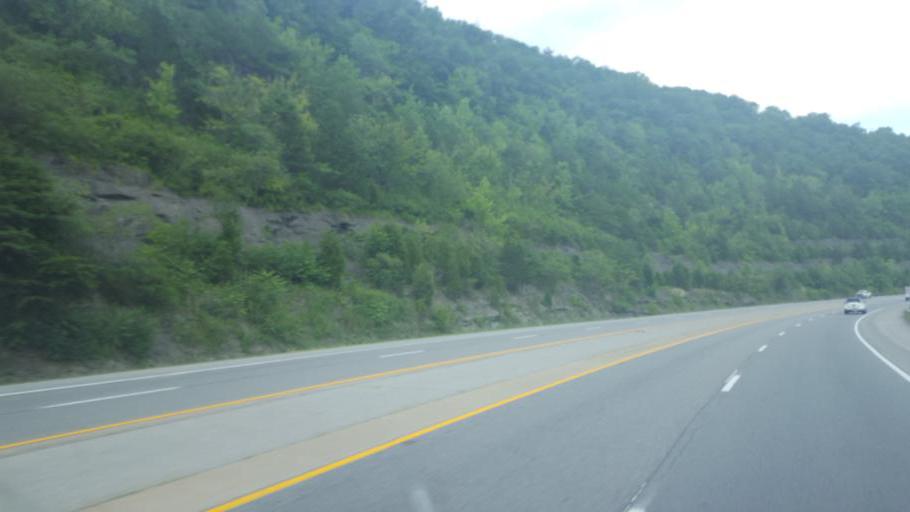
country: US
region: Kentucky
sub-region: Pike County
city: Pikeville
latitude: 37.4648
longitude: -82.5206
